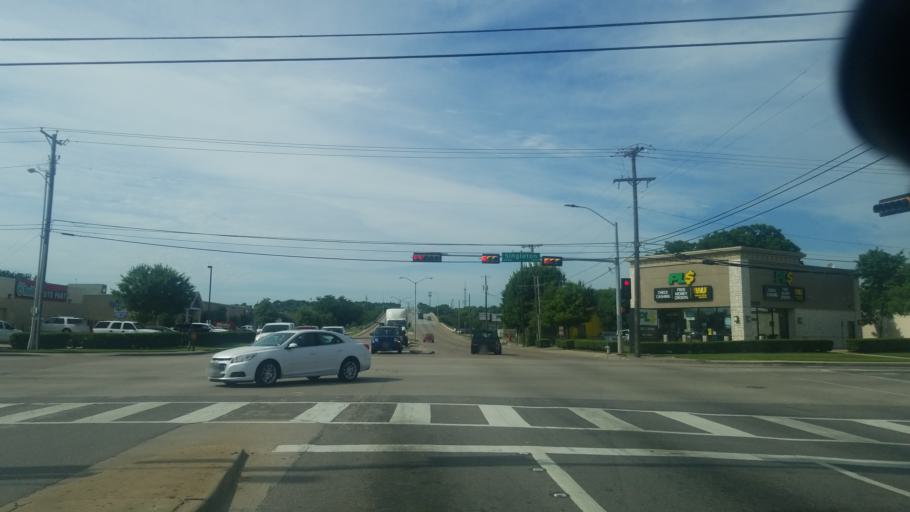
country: US
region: Texas
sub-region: Dallas County
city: Dallas
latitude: 32.7790
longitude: -96.8565
